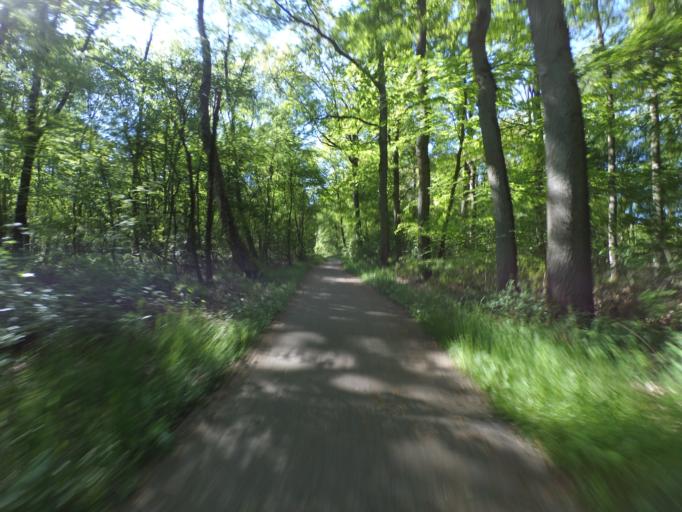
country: NL
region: Gelderland
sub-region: Gemeente Brummen
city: Brummen
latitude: 52.1050
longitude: 6.1125
